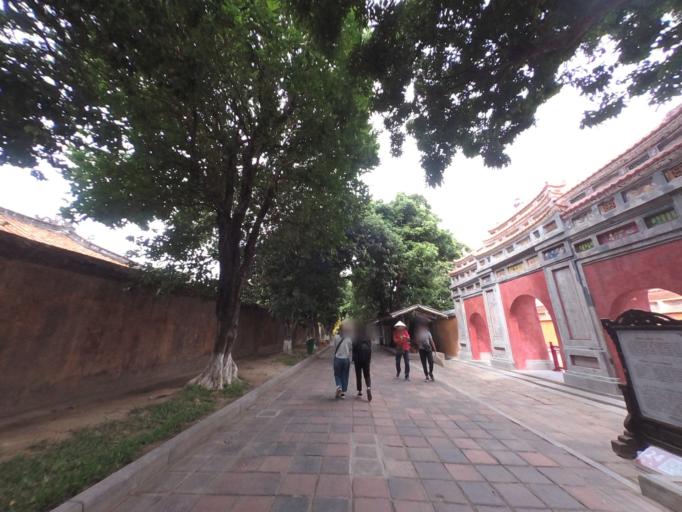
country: VN
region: Thua Thien-Hue
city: Hue
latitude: 16.4678
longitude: 107.5765
